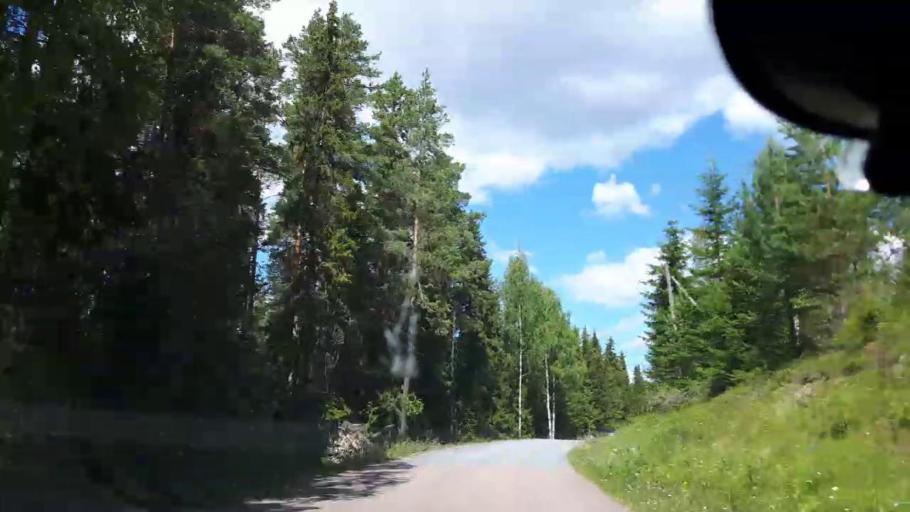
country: SE
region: Jaemtland
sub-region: Ragunda Kommun
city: Hammarstrand
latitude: 62.9389
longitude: 16.6917
